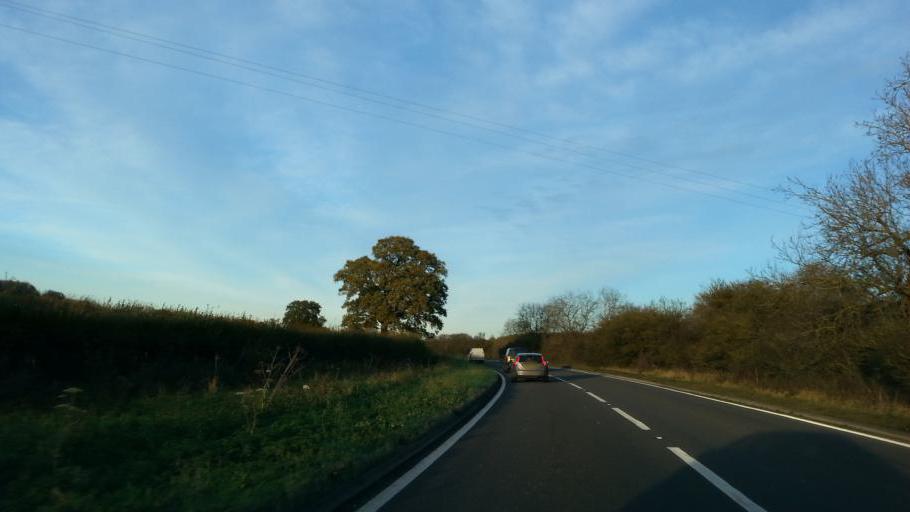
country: GB
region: England
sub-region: District of Rutland
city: South Luffenham
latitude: 52.5534
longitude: -0.5788
